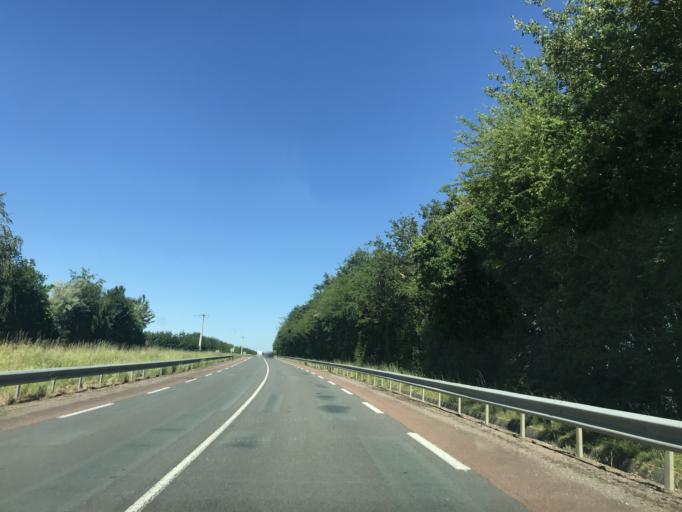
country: FR
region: Poitou-Charentes
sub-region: Departement de la Charente-Maritime
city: Gemozac
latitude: 45.5739
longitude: -0.6600
